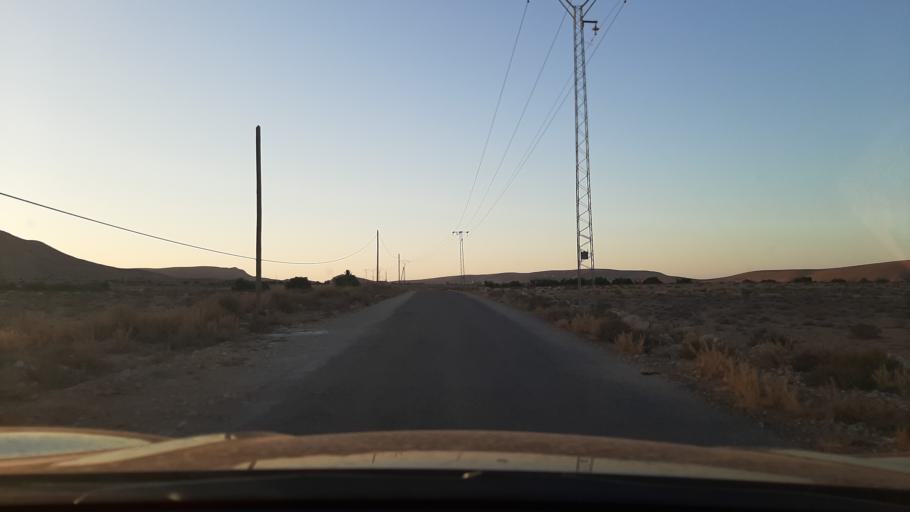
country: TN
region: Qabis
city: Matmata
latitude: 33.5464
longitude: 10.1915
